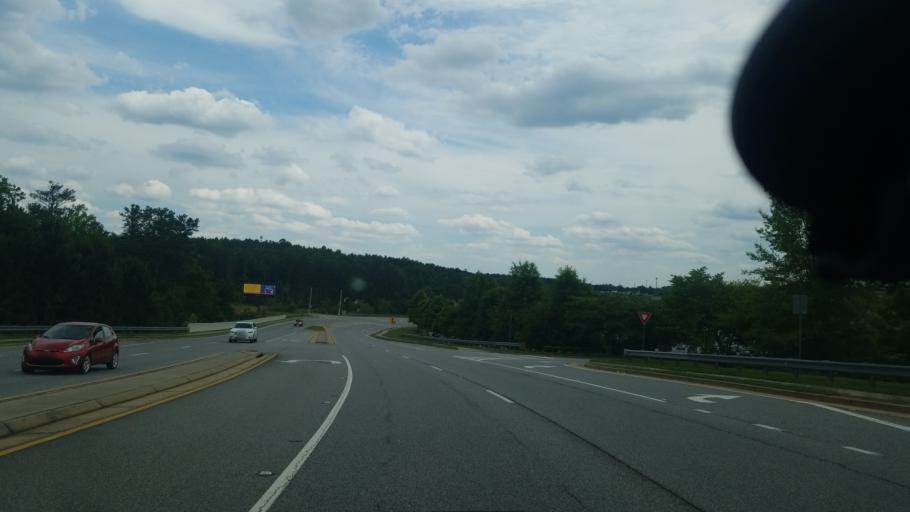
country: US
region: Georgia
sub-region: Forsyth County
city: Cumming
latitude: 34.1964
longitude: -84.1268
